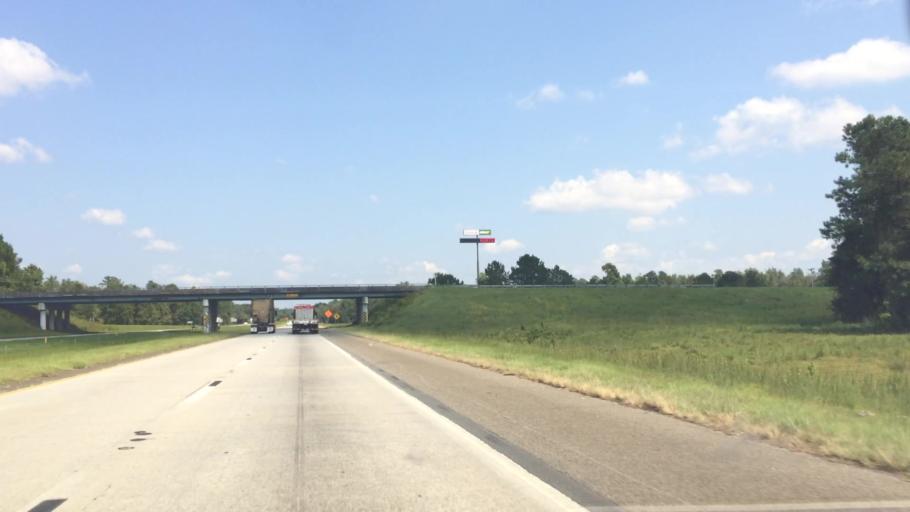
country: US
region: South Carolina
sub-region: Dorchester County
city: Saint George
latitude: 33.0831
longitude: -80.6533
